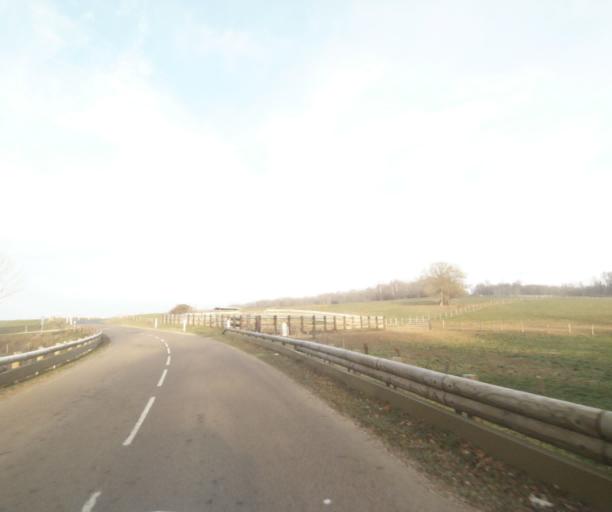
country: FR
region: Champagne-Ardenne
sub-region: Departement de la Marne
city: Sermaize-les-Bains
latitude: 48.7456
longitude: 4.9062
